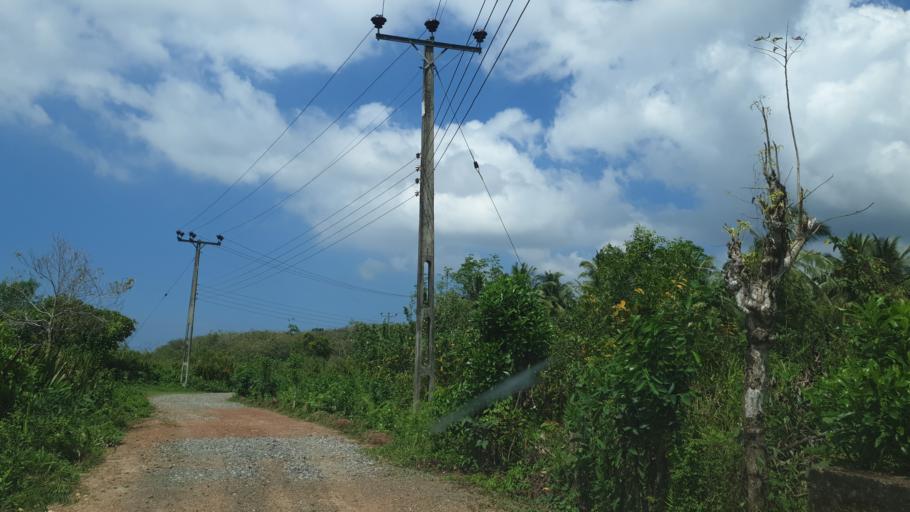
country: LK
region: Western
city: Panadura
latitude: 6.6776
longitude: 79.9619
